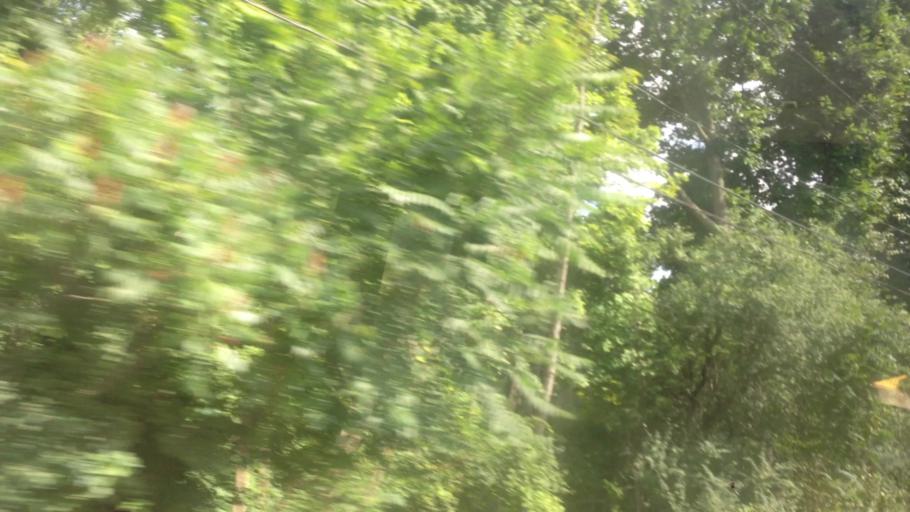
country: US
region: New York
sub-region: Dutchess County
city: Red Hook
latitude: 41.9984
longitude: -73.9129
